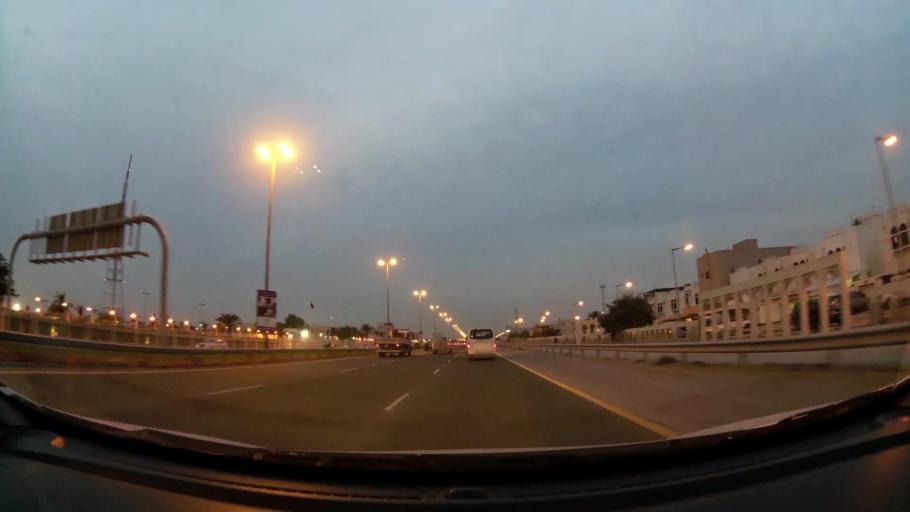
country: BH
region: Northern
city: Madinat `Isa
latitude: 26.1641
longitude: 50.5572
